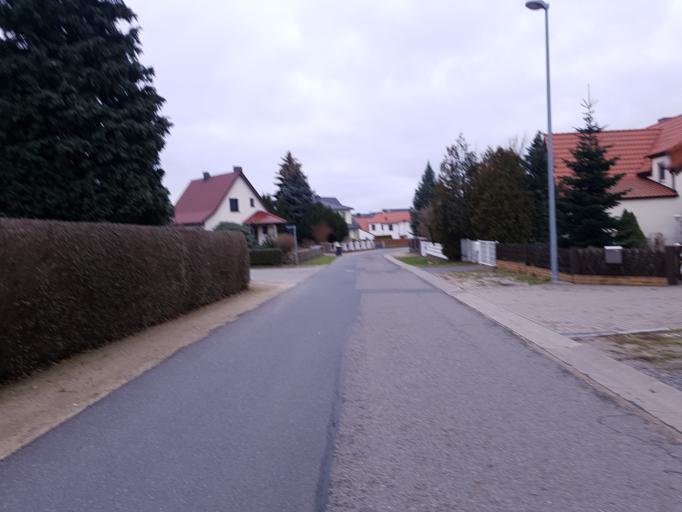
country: DE
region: Brandenburg
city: Groden
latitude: 51.4042
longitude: 13.5767
